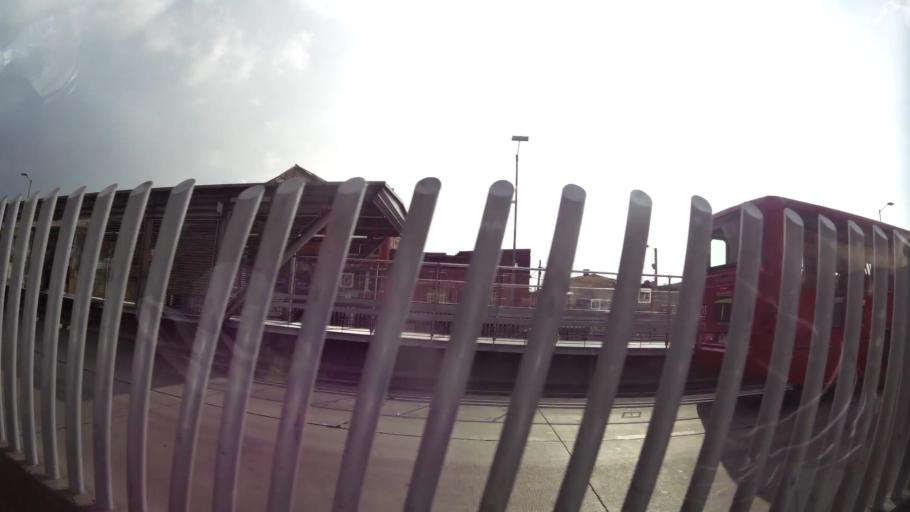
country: CO
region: Bogota D.C.
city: Bogota
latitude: 4.5601
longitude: -74.1237
